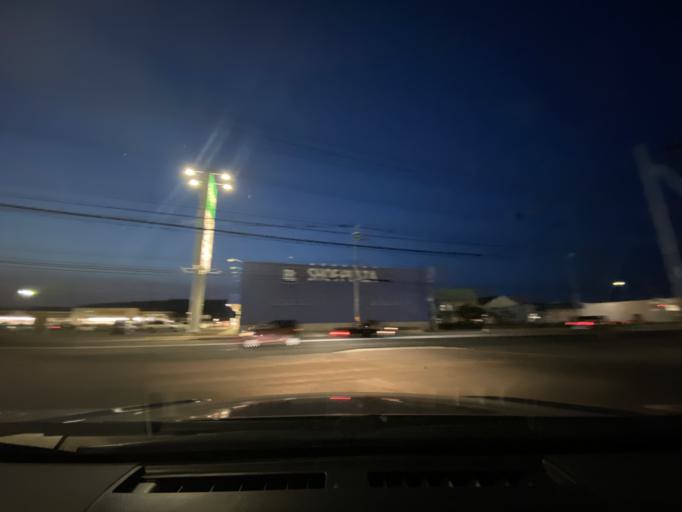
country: JP
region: Hokkaido
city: Kitami
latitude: 43.7975
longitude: 143.8532
